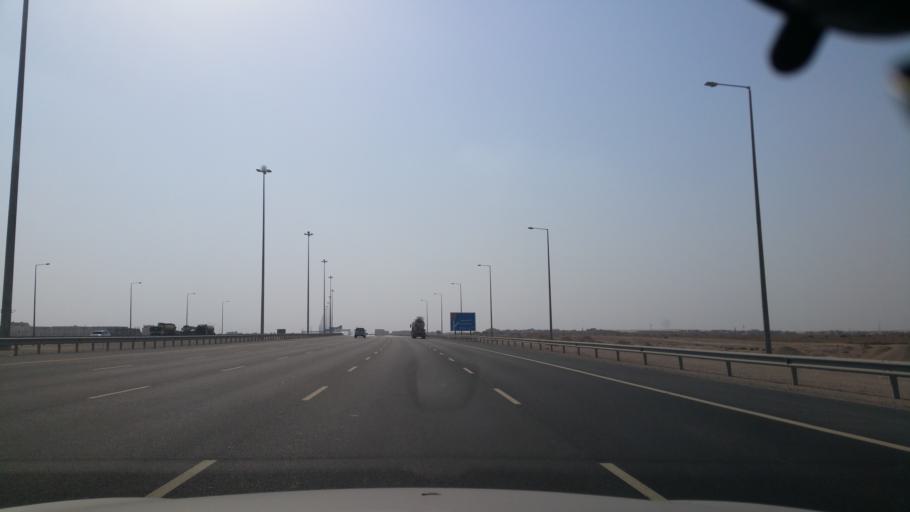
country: QA
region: Baladiyat Umm Salal
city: Umm Salal `Ali
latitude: 25.4568
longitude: 51.4418
